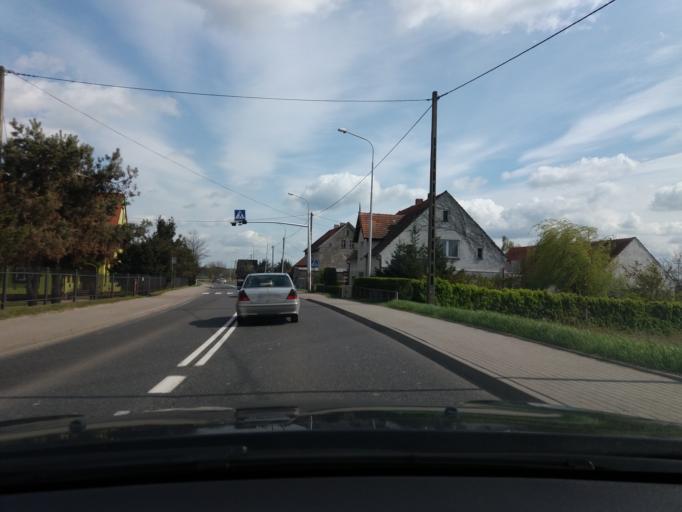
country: PL
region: Lower Silesian Voivodeship
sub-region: Powiat sredzki
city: Malczyce
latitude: 51.1996
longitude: 16.4824
